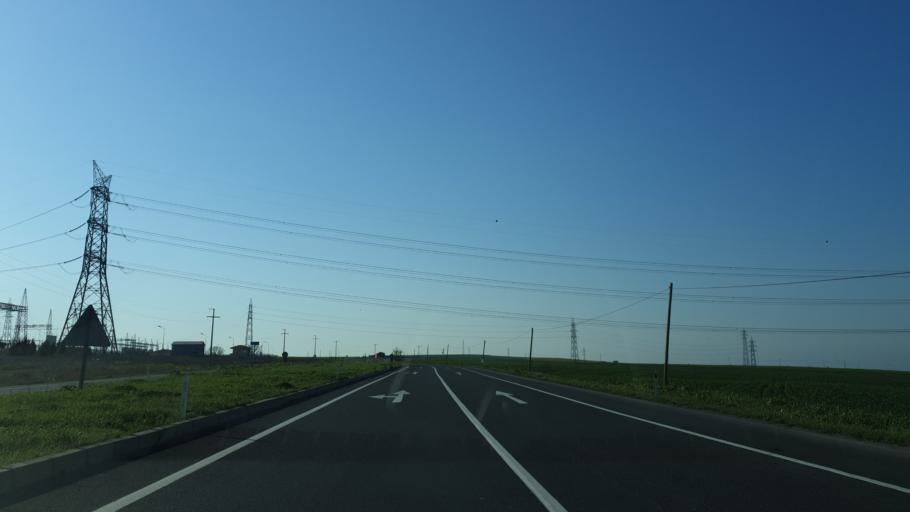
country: TR
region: Tekirdag
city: Corlu
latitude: 41.1062
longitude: 27.7513
